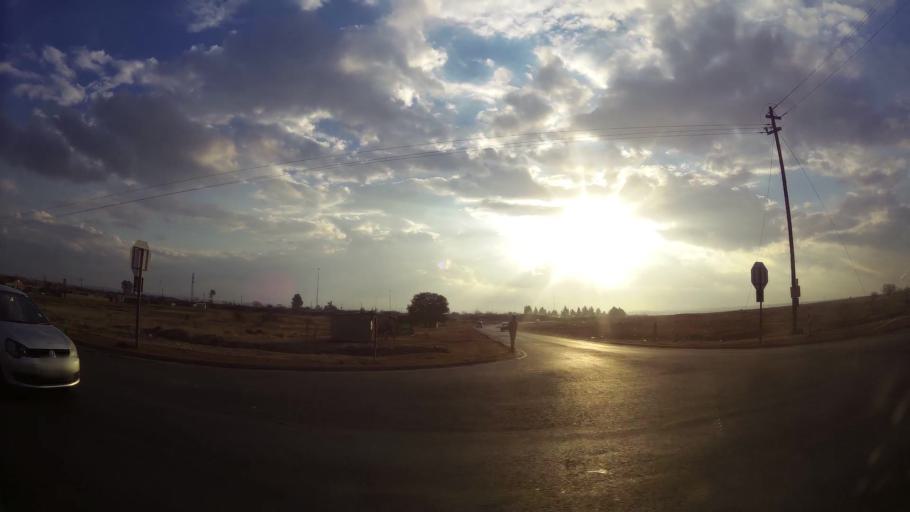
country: ZA
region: Gauteng
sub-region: Sedibeng District Municipality
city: Vanderbijlpark
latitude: -26.6020
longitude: 27.8181
